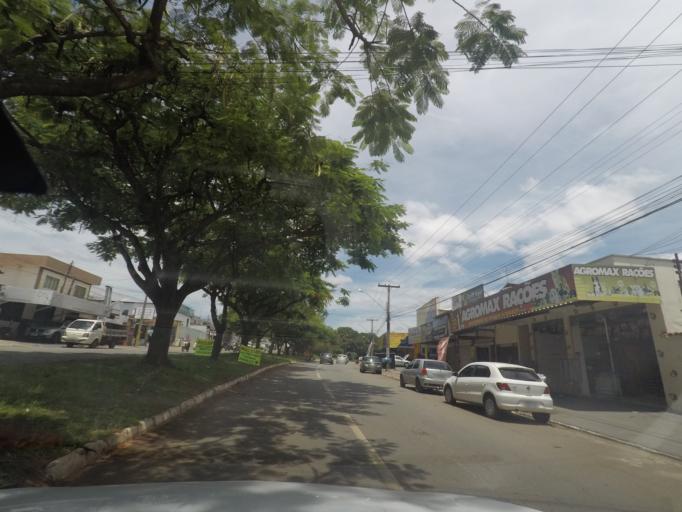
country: BR
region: Goias
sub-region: Goiania
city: Goiania
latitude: -16.6681
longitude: -49.2188
